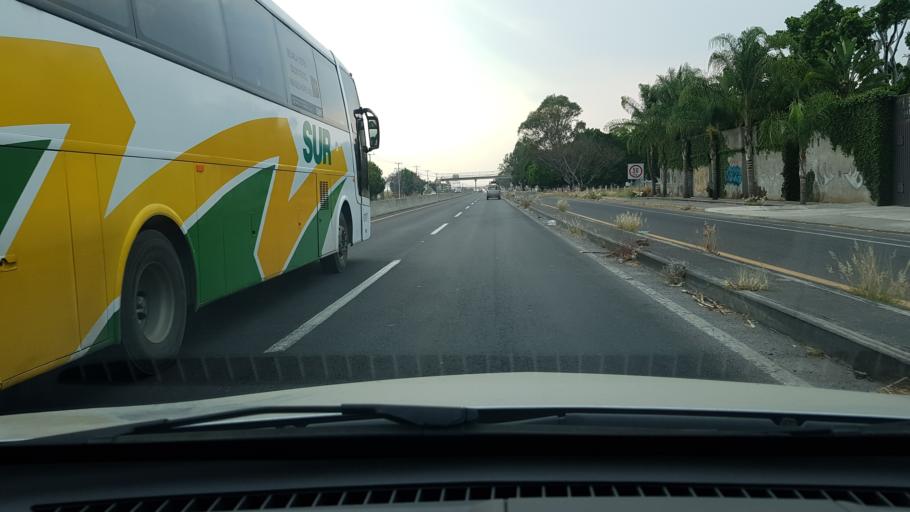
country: MX
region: Morelos
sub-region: Ayala
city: Unidad Habitacional Mariano Matamoros
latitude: 18.7474
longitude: -98.8446
